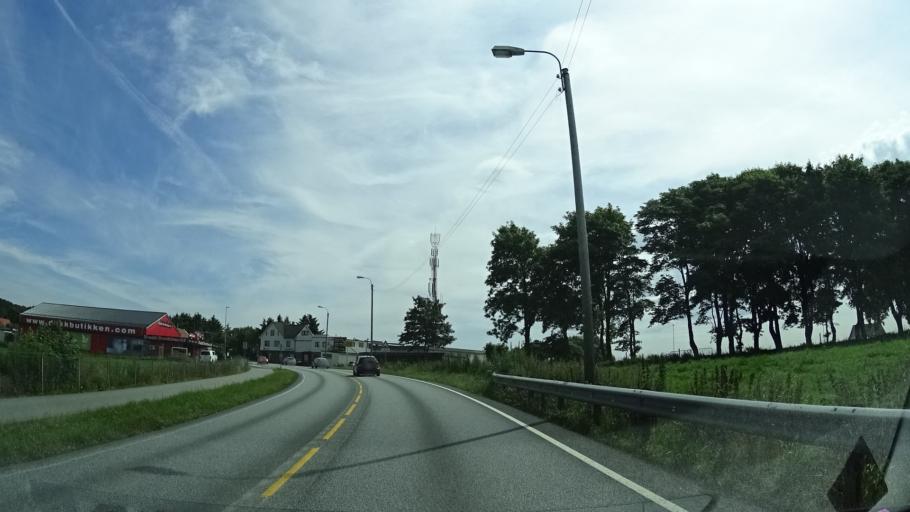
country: NO
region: Rogaland
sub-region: Randaberg
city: Randaberg
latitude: 58.9836
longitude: 5.6670
